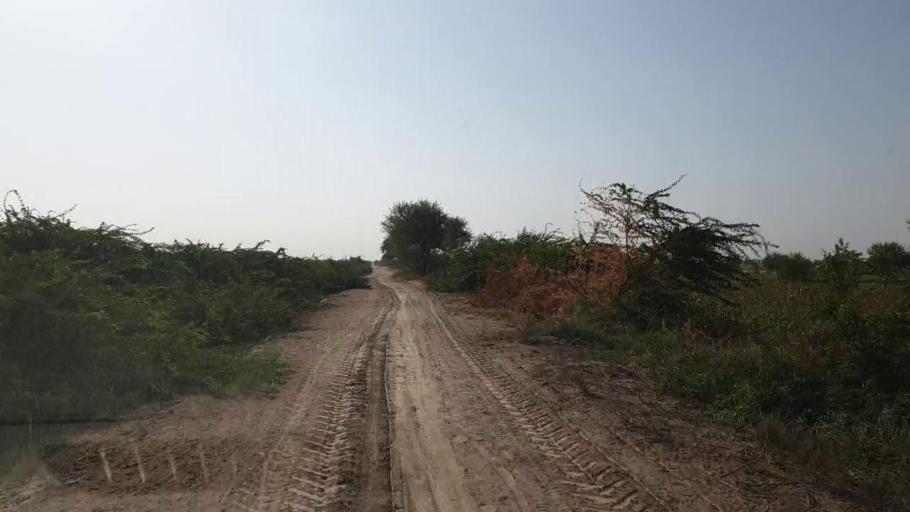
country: PK
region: Sindh
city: Kadhan
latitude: 24.5860
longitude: 69.0781
